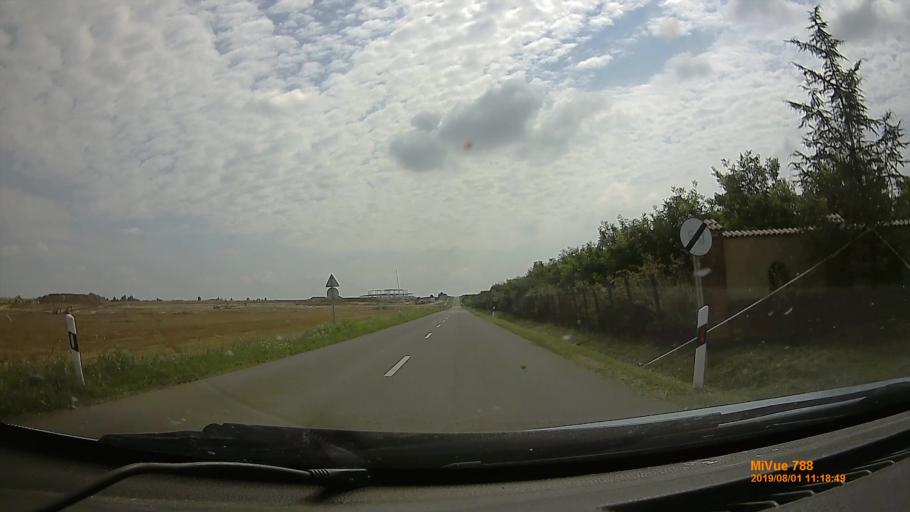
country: HU
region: Baranya
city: Pellerd
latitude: 46.0108
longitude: 18.2185
